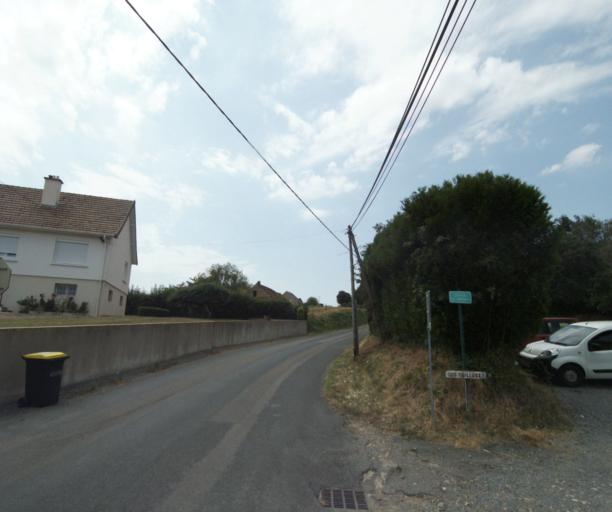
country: FR
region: Bourgogne
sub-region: Departement de Saone-et-Loire
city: Gueugnon
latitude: 46.5996
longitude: 4.0239
